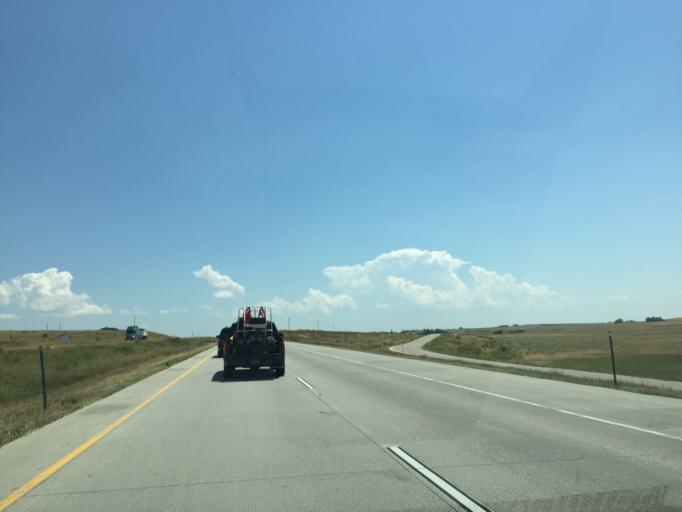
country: US
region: Colorado
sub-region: Lincoln County
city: Limon
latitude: 39.4900
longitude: -103.9580
